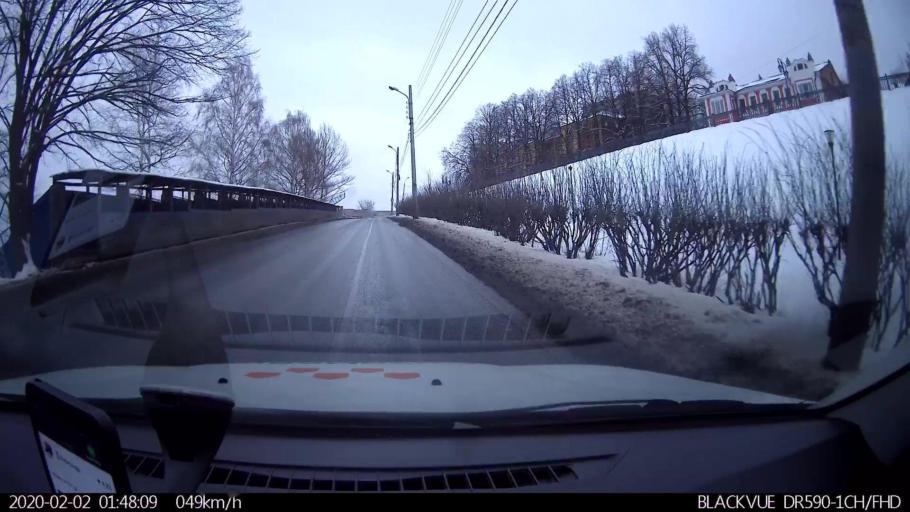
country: RU
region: Nizjnij Novgorod
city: Nizhniy Novgorod
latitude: 56.3306
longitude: 44.0367
